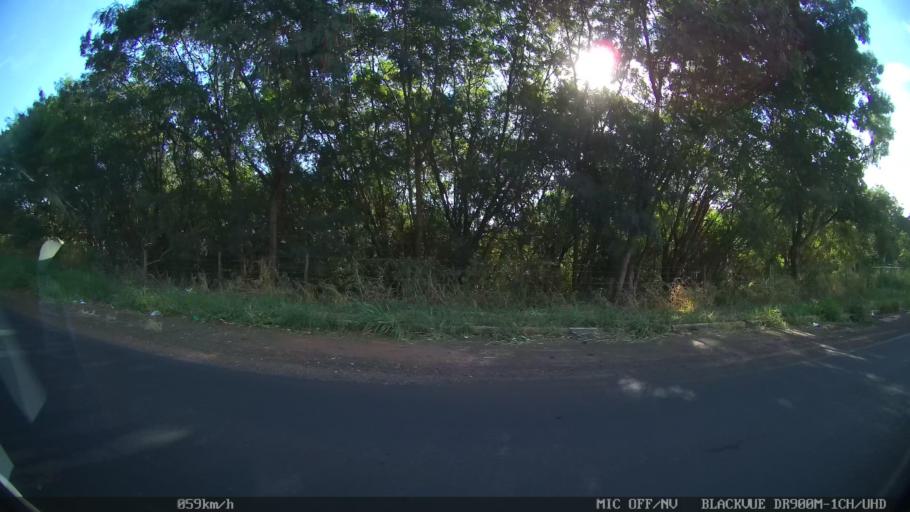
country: BR
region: Sao Paulo
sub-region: Americo Brasiliense
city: Americo Brasiliense
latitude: -21.7575
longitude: -48.1397
